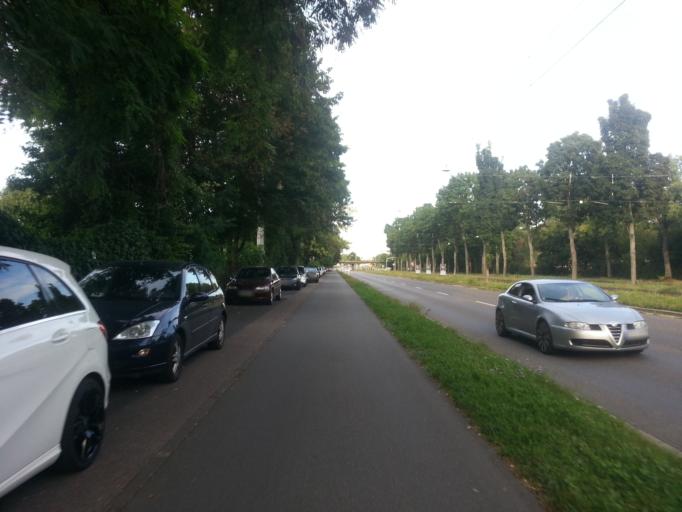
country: DE
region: Baden-Wuerttemberg
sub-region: Karlsruhe Region
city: Mannheim
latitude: 49.4894
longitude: 8.5062
